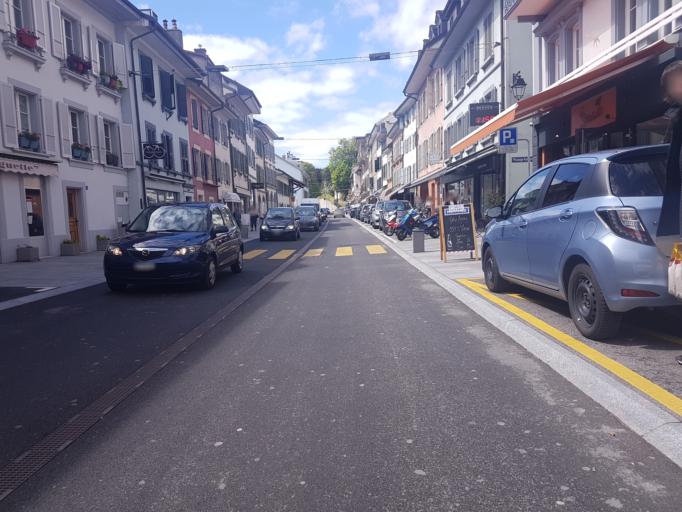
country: CH
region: Vaud
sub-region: Nyon District
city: Rolle
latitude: 46.4573
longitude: 6.3378
